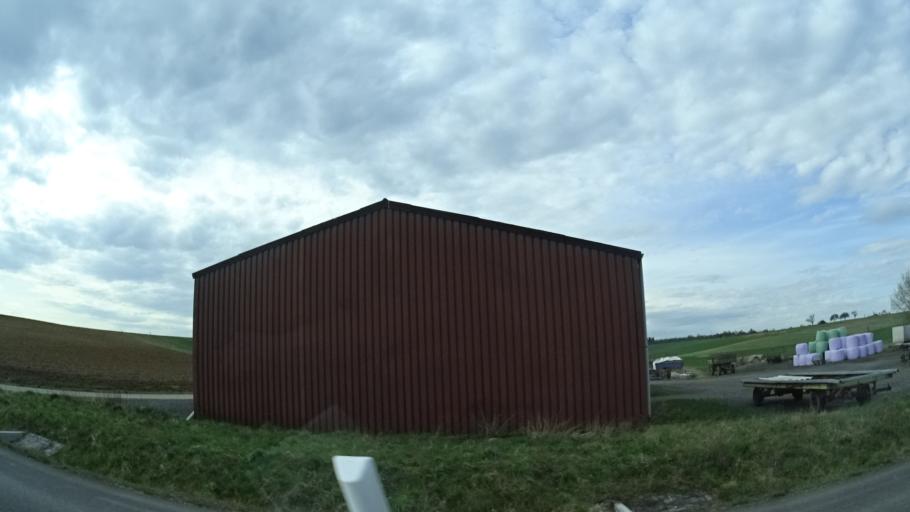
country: DE
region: Hesse
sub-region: Regierungsbezirk Darmstadt
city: Hammersbach
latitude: 50.2516
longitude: 9.0174
